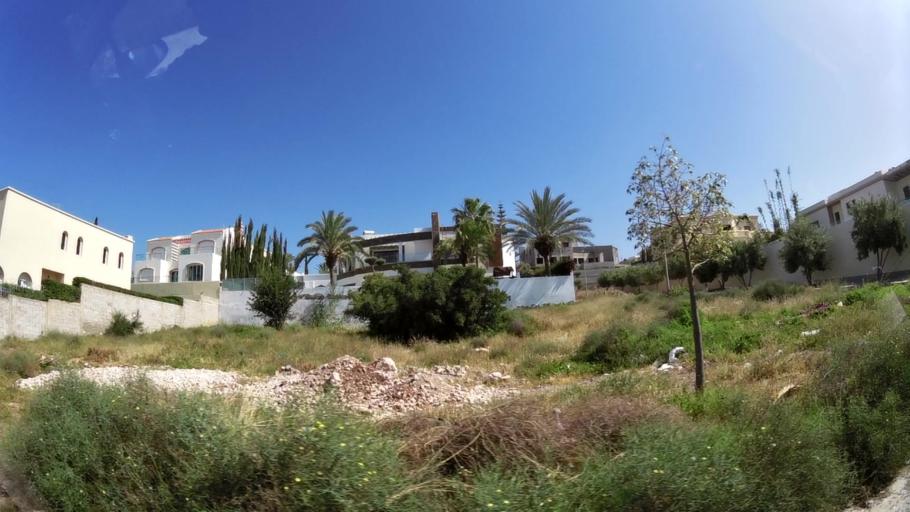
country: MA
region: Souss-Massa-Draa
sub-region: Agadir-Ida-ou-Tnan
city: Agadir
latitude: 30.4421
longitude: -9.5840
